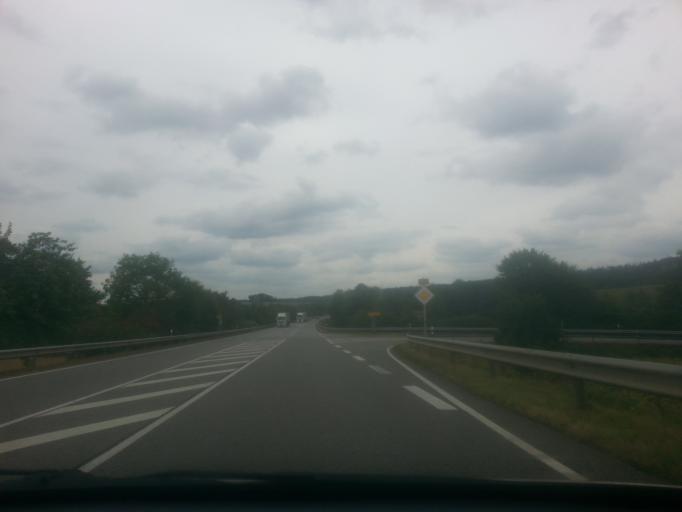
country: DE
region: Bavaria
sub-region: Lower Bavaria
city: Pfeffenhausen
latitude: 48.6697
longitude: 11.9419
